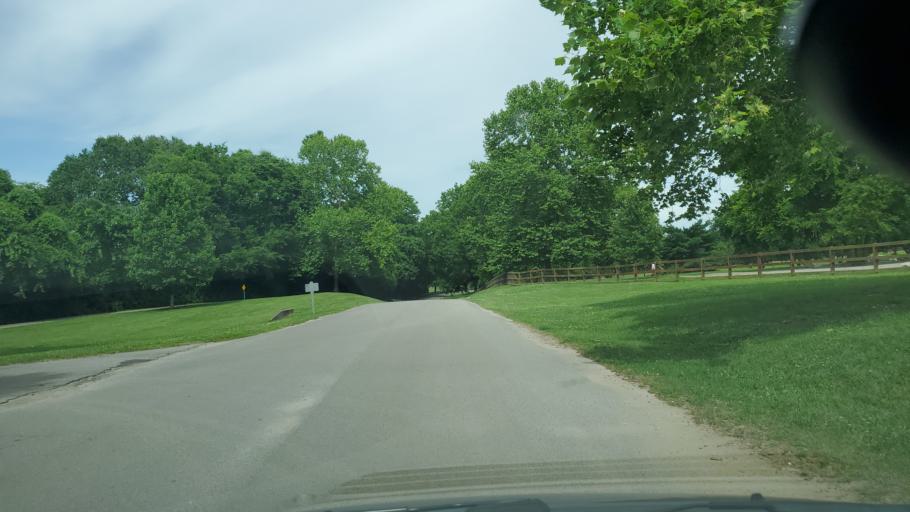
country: US
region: Tennessee
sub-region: Davidson County
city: Lakewood
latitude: 36.1917
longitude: -86.6777
